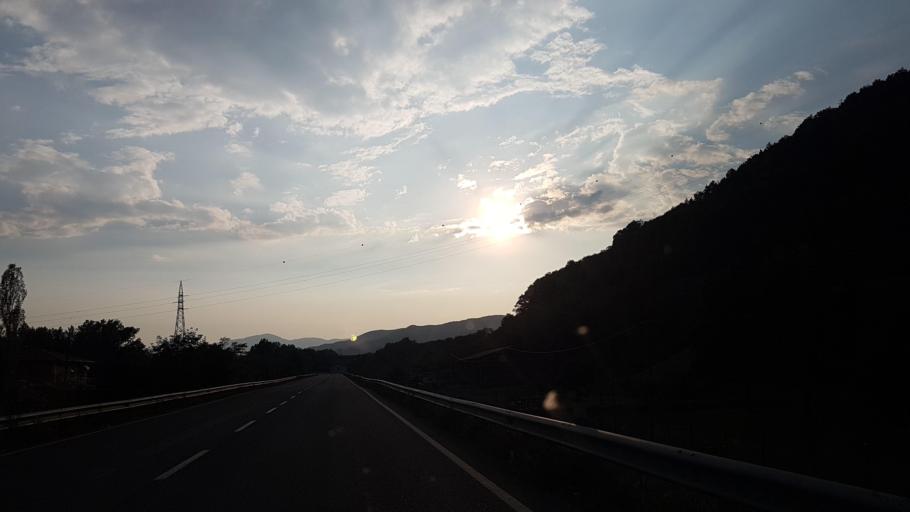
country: IT
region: Emilia-Romagna
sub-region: Provincia di Parma
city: Borgo Val di Taro
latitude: 44.4955
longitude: 9.7905
